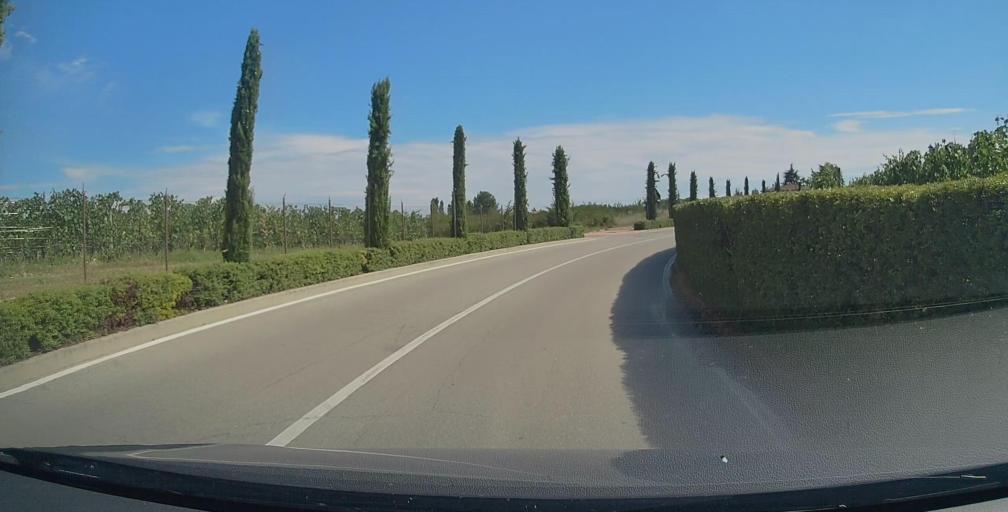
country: IT
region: Lombardy
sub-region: Provincia di Brescia
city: San Martino della Battaglia
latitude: 45.4532
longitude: 10.6167
